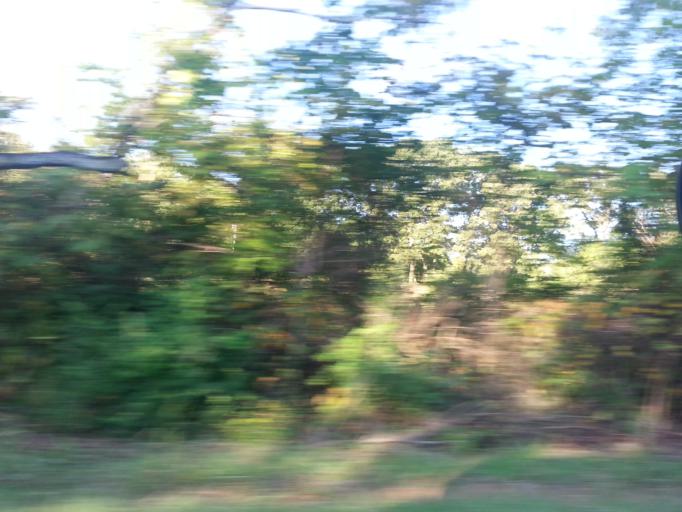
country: US
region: Tennessee
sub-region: Blount County
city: Eagleton Village
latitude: 35.7841
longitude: -83.9379
